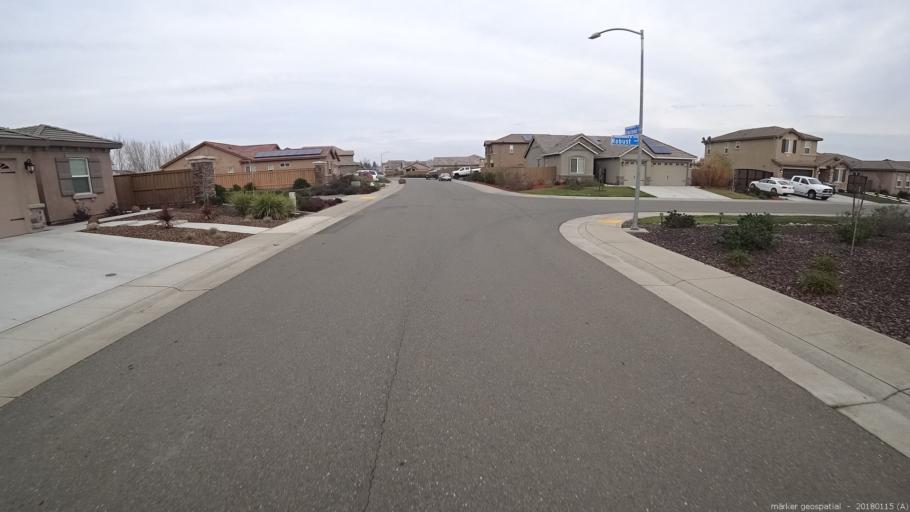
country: US
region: California
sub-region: Sacramento County
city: Rancho Cordova
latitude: 38.5775
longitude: -121.2705
